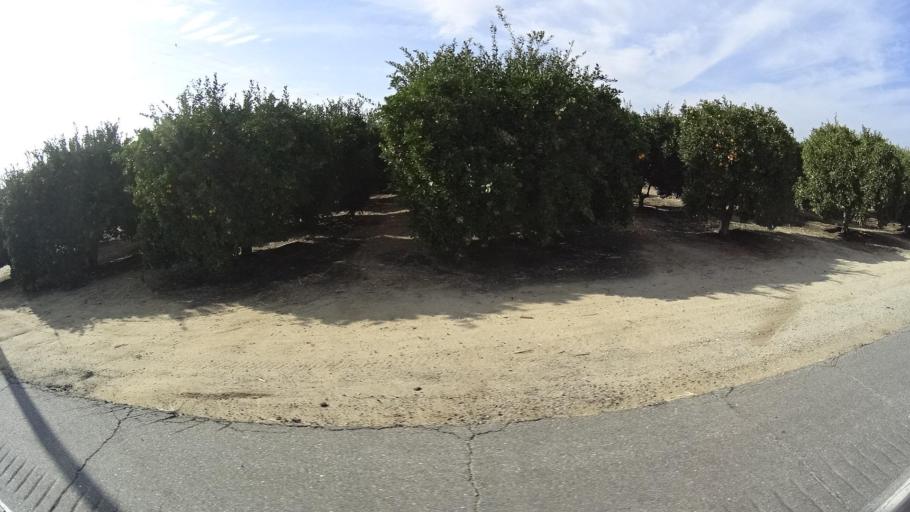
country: US
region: California
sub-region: Kern County
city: Lamont
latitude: 35.3184
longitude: -118.8431
